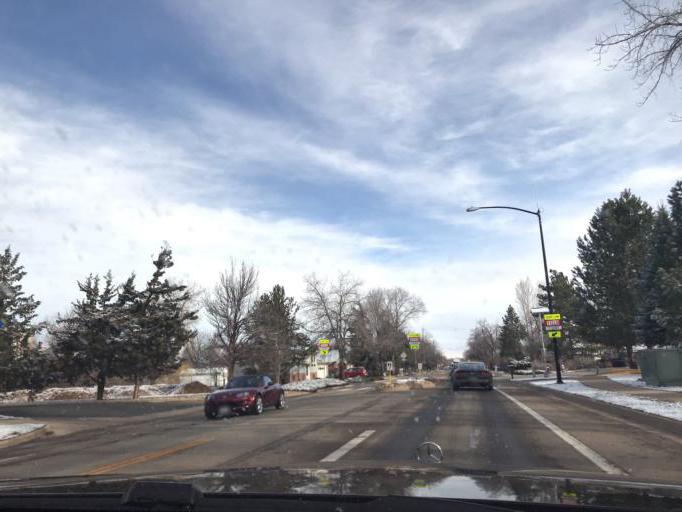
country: US
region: Colorado
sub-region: Boulder County
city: Boulder
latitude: 40.0106
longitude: -105.2253
